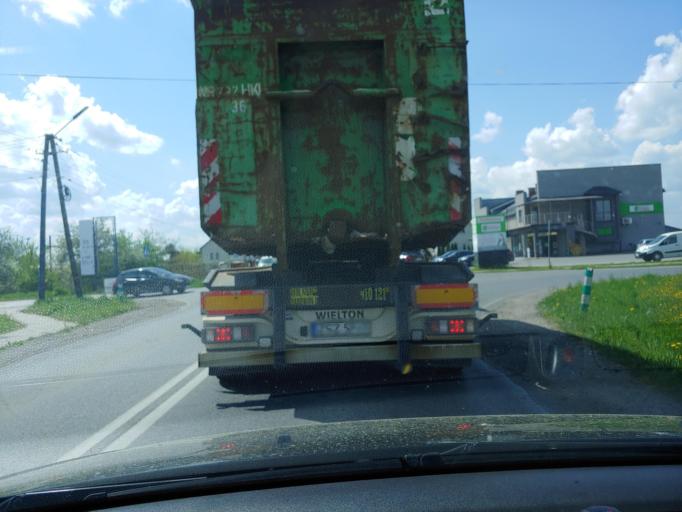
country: PL
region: Subcarpathian Voivodeship
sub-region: Powiat mielecki
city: Mielec
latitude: 50.2816
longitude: 21.3891
